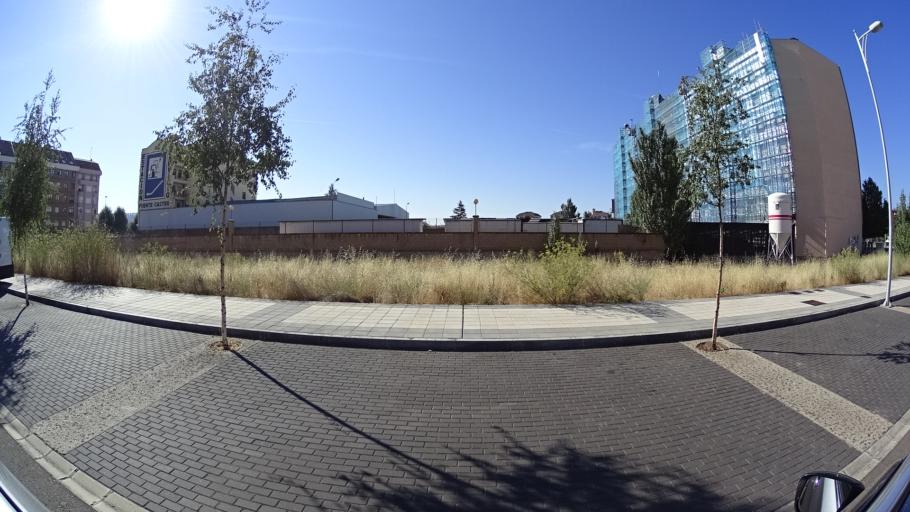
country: ES
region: Castille and Leon
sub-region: Provincia de Leon
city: Leon
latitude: 42.5862
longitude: -5.5607
